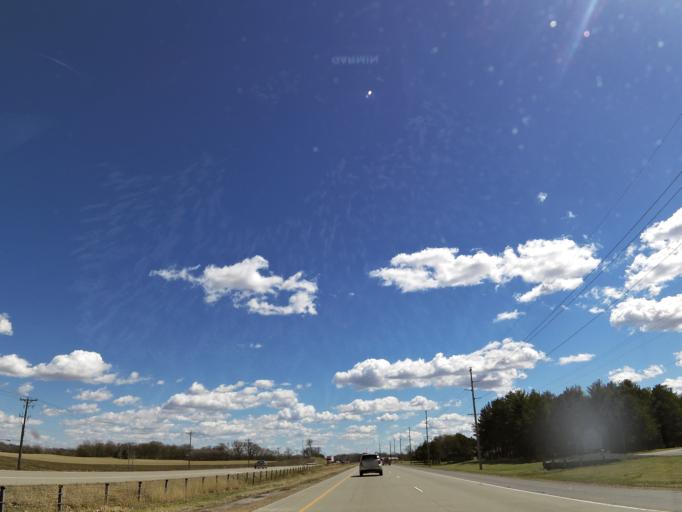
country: US
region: Minnesota
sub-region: Dakota County
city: Hastings
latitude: 44.7900
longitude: -92.8838
